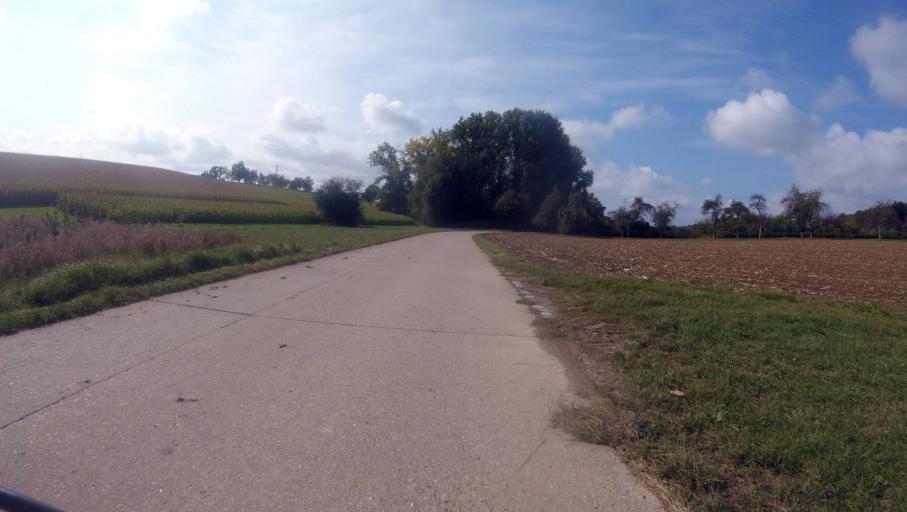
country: DE
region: Baden-Wuerttemberg
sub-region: Regierungsbezirk Stuttgart
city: Affalterbach
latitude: 48.9010
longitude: 9.3333
